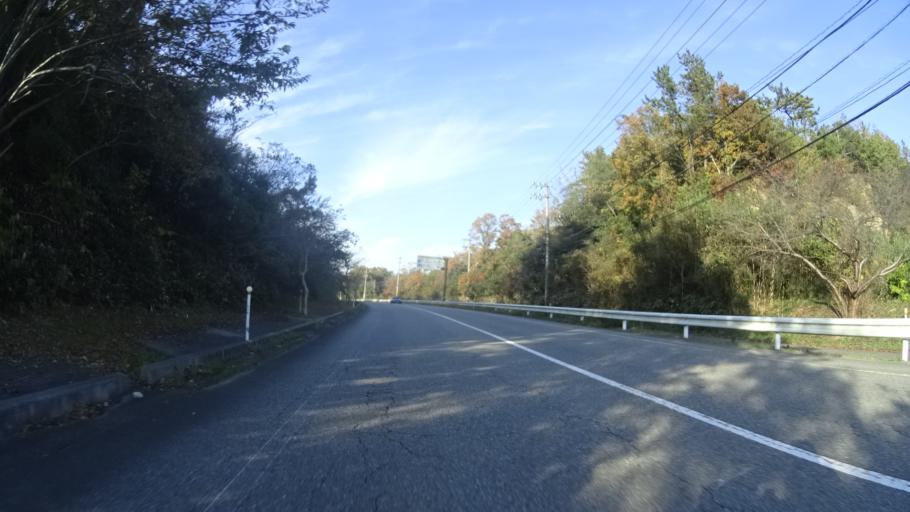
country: JP
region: Ishikawa
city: Hakui
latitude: 37.0375
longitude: 136.7788
